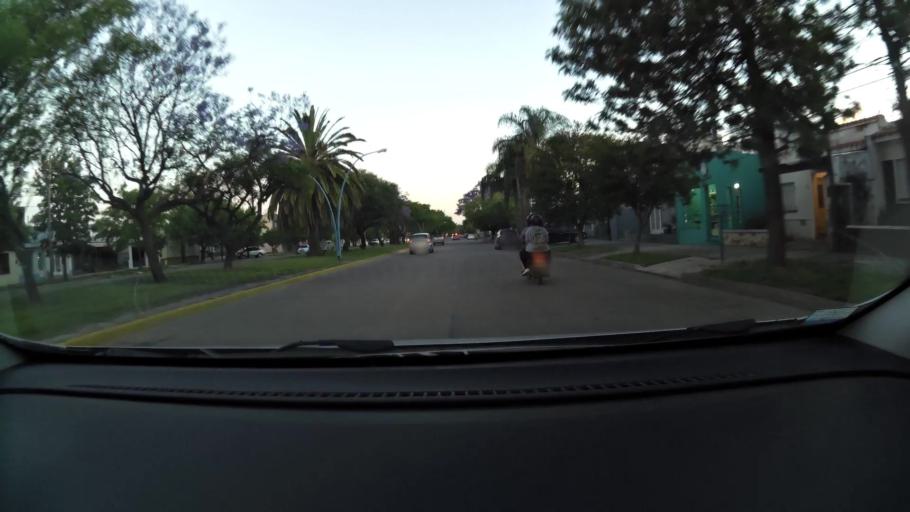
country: AR
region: Cordoba
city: Villa Maria
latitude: -32.4189
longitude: -63.2481
